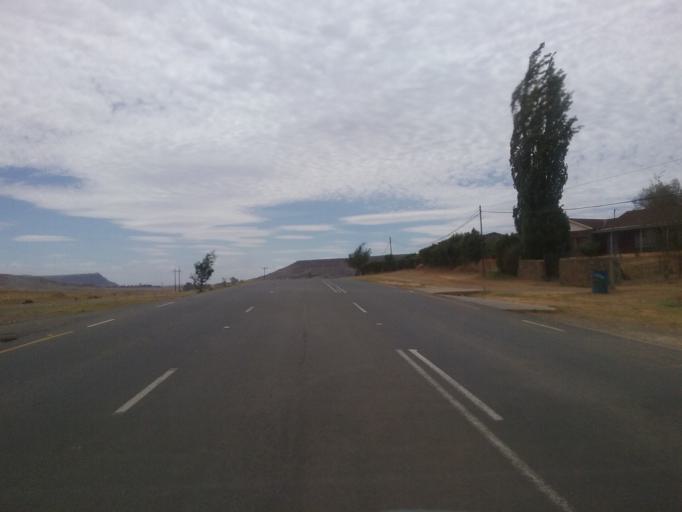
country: LS
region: Maseru
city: Nako
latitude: -29.6327
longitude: 27.4813
